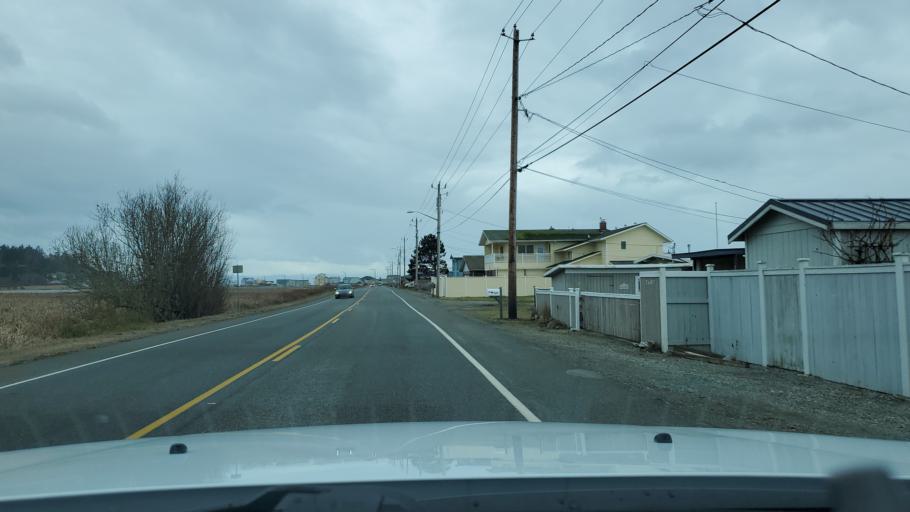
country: US
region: Washington
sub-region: Island County
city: Ault Field
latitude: 48.3074
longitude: -122.7174
